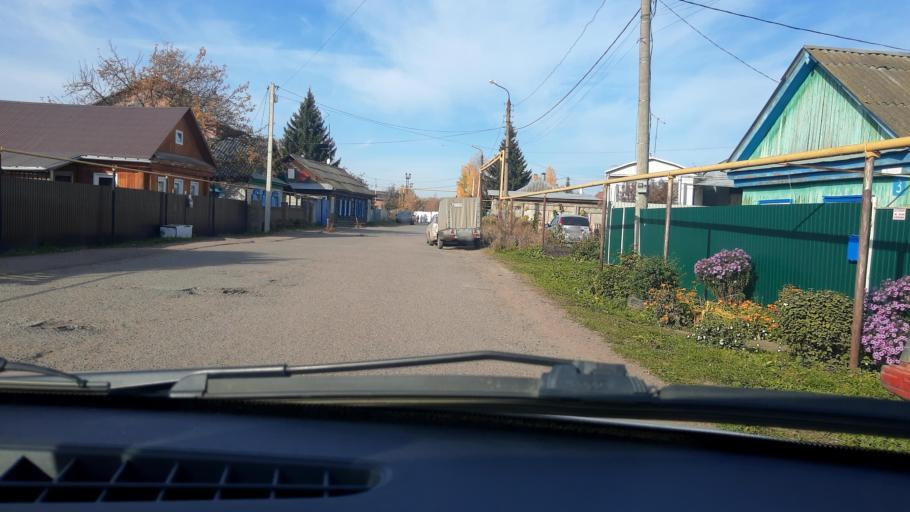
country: RU
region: Bashkortostan
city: Ufa
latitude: 54.7819
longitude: 56.0602
